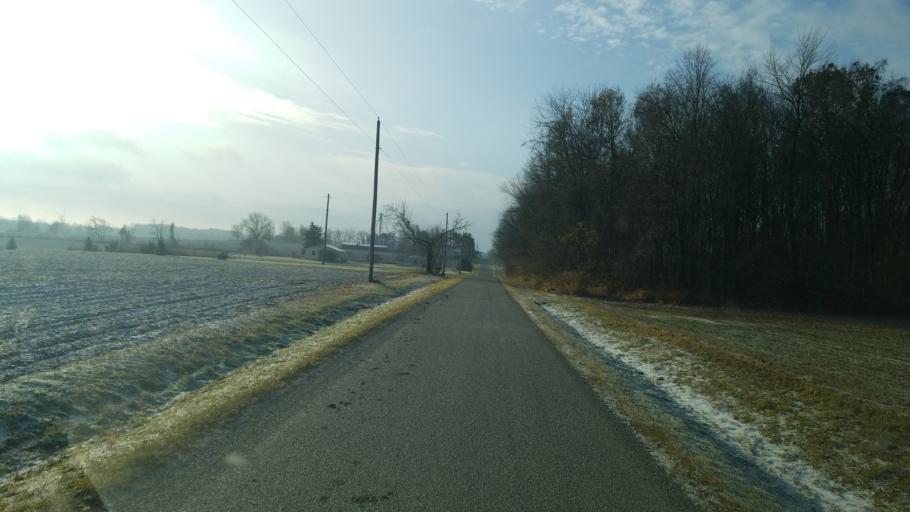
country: US
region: Ohio
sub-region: Richland County
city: Shelby
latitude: 40.9158
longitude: -82.7627
